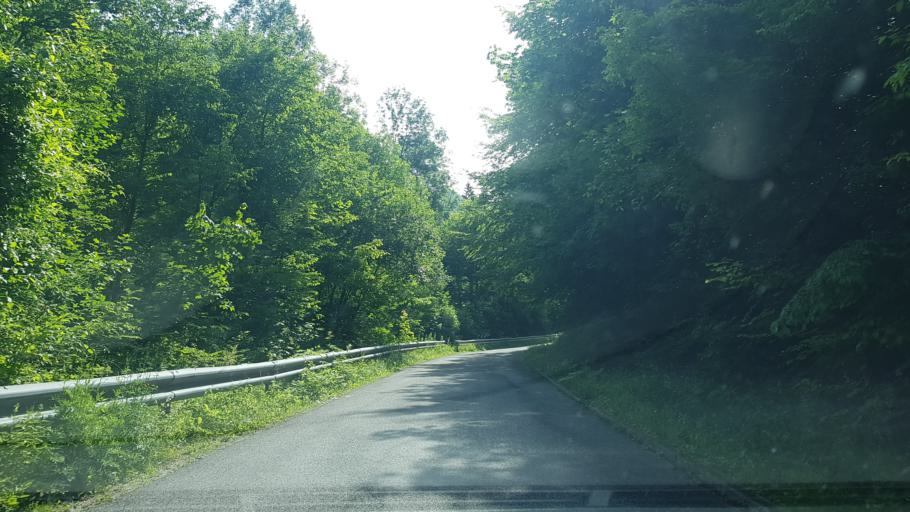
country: SI
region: Velenje
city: Velenje
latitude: 46.3884
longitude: 15.1666
